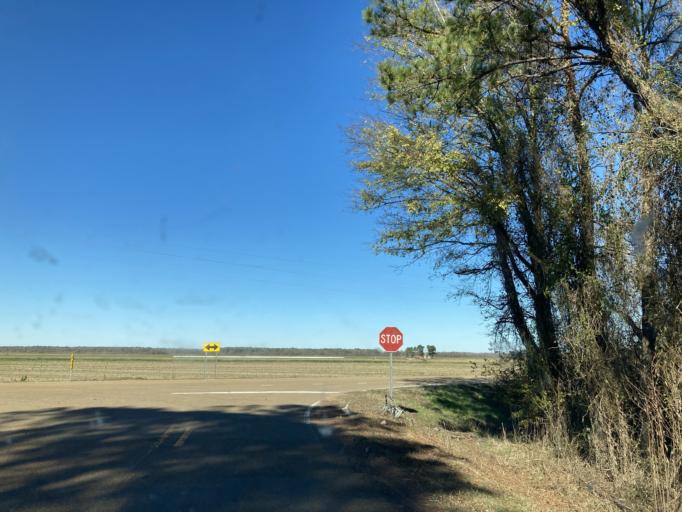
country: US
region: Mississippi
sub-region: Hinds County
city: Lynchburg
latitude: 32.6213
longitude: -90.5750
